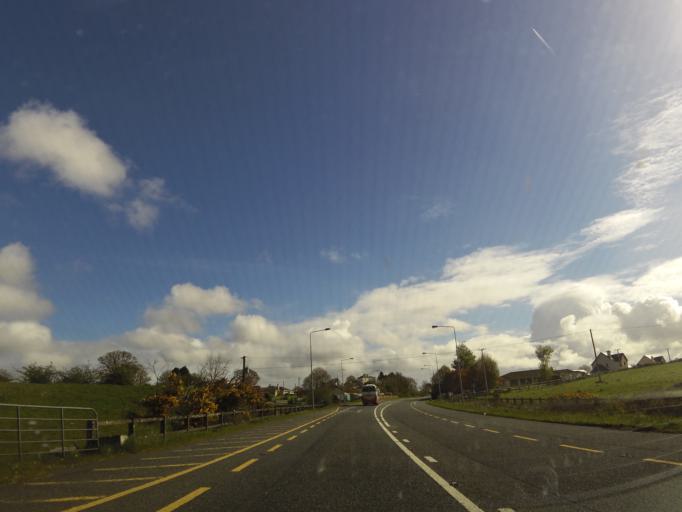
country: IE
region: Connaught
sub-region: Maigh Eo
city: Swinford
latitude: 53.8720
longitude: -8.8456
